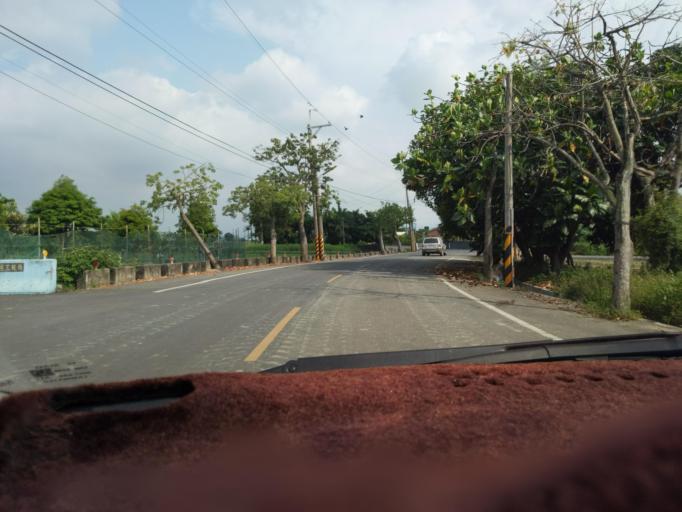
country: TW
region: Taiwan
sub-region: Yunlin
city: Douliu
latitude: 23.7892
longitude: 120.4000
